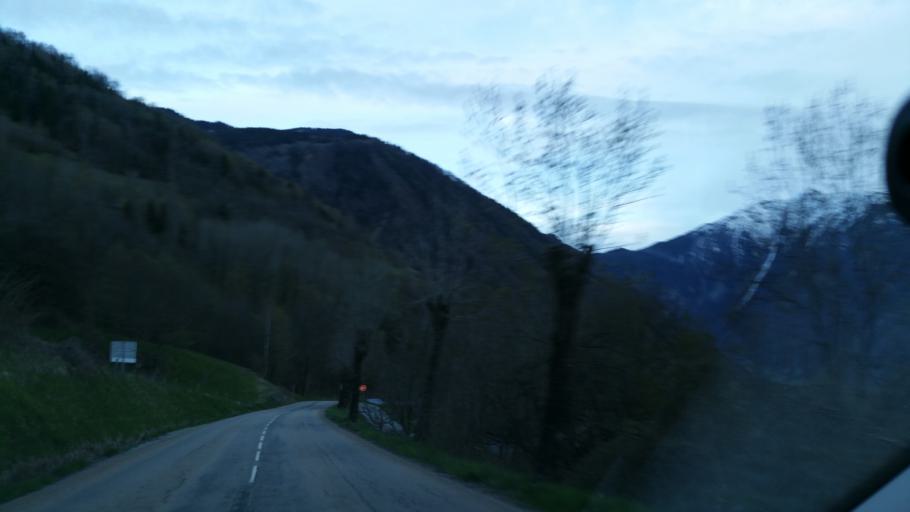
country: FR
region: Rhone-Alpes
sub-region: Departement de la Savoie
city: La Chambre
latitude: 45.3735
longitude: 6.3212
